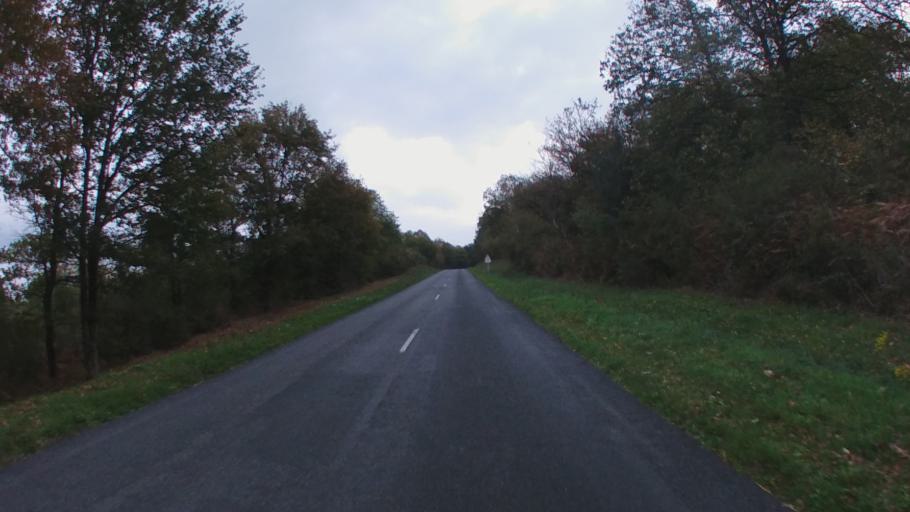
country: FR
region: Pays de la Loire
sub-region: Departement de Maine-et-Loire
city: Distre
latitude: 47.2594
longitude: -0.1237
